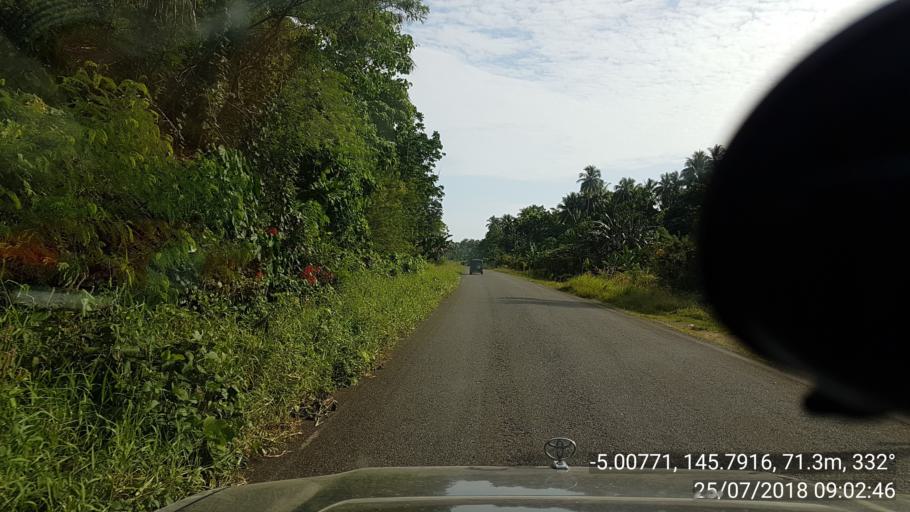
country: PG
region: Madang
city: Madang
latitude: -5.0078
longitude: 145.7917
